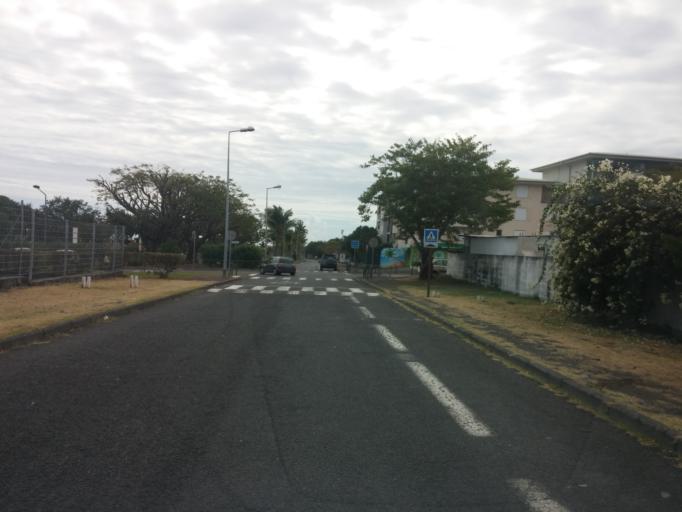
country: RE
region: Reunion
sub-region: Reunion
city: Le Port
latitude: -20.9497
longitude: 55.2941
